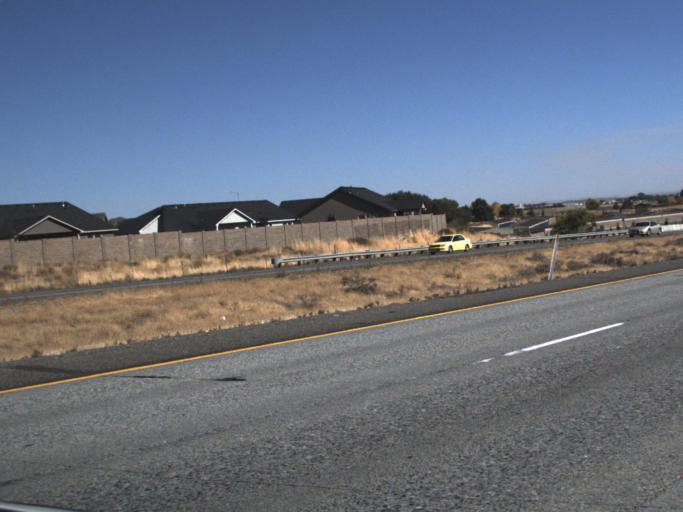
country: US
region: Washington
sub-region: Franklin County
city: West Pasco
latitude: 46.2571
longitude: -119.1553
